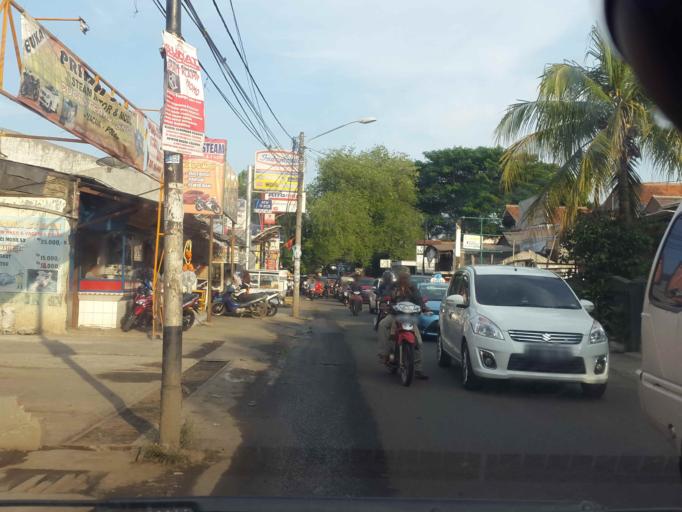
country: ID
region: West Java
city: Ciputat
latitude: -6.2445
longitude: 106.6976
